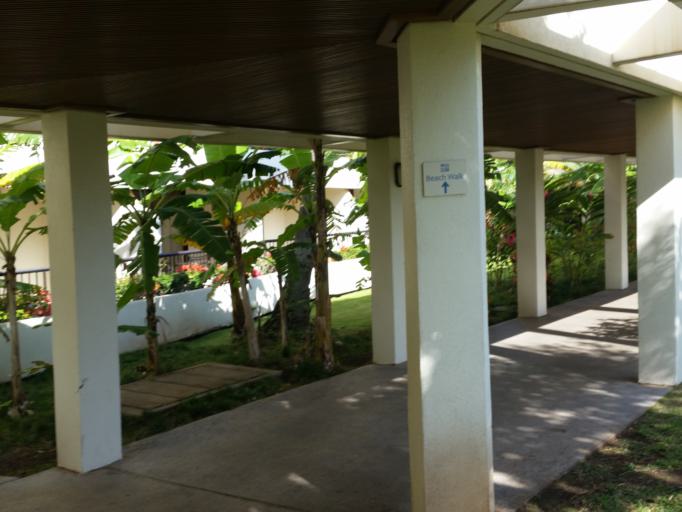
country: US
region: Hawaii
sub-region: Maui County
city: Ka'anapali
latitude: 20.9274
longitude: -156.6945
